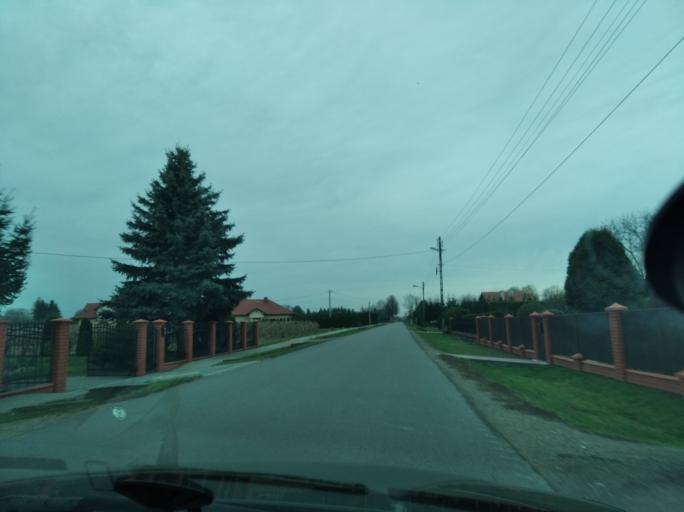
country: PL
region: Subcarpathian Voivodeship
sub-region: Powiat lancucki
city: Czarna
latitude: 50.0989
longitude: 22.2076
